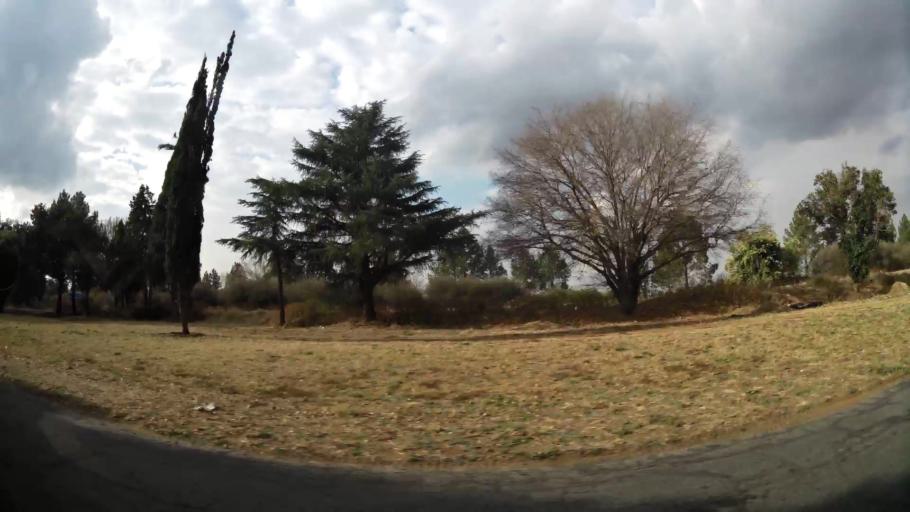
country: ZA
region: Orange Free State
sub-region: Fezile Dabi District Municipality
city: Sasolburg
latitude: -26.8089
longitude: 27.8371
